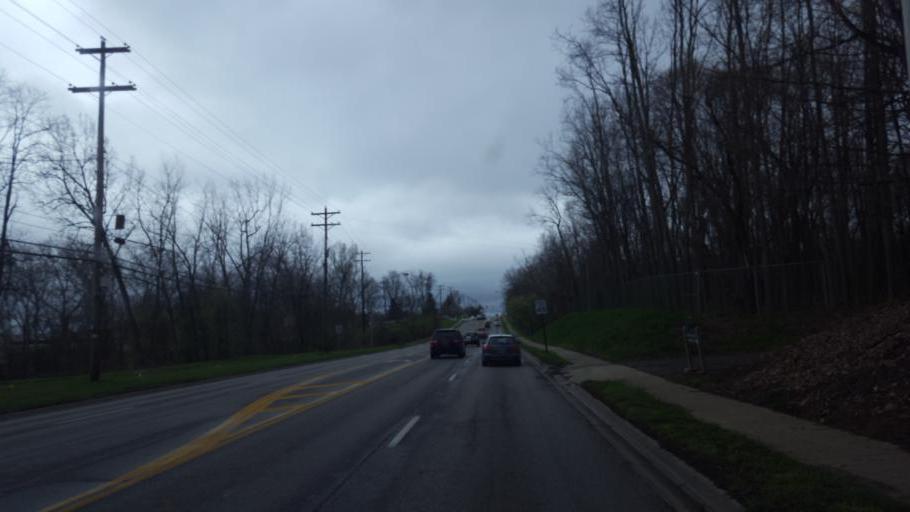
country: US
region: Ohio
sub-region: Franklin County
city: Westerville
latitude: 40.1193
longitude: -82.9486
